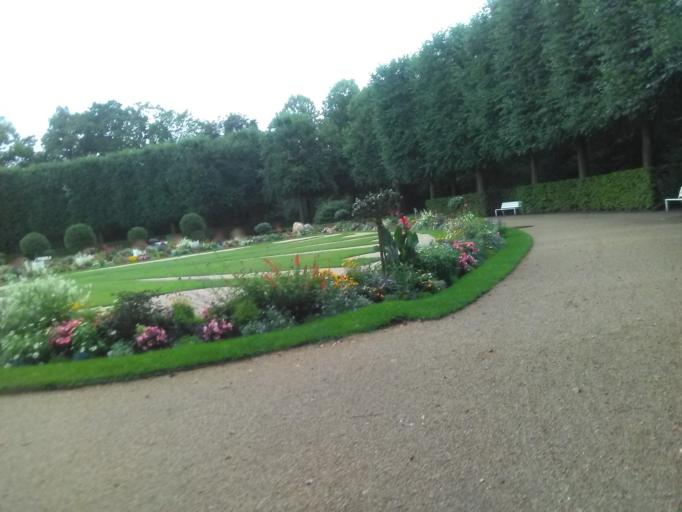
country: DE
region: Bavaria
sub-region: Regierungsbezirk Mittelfranken
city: Ansbach
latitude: 49.3015
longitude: 10.5798
